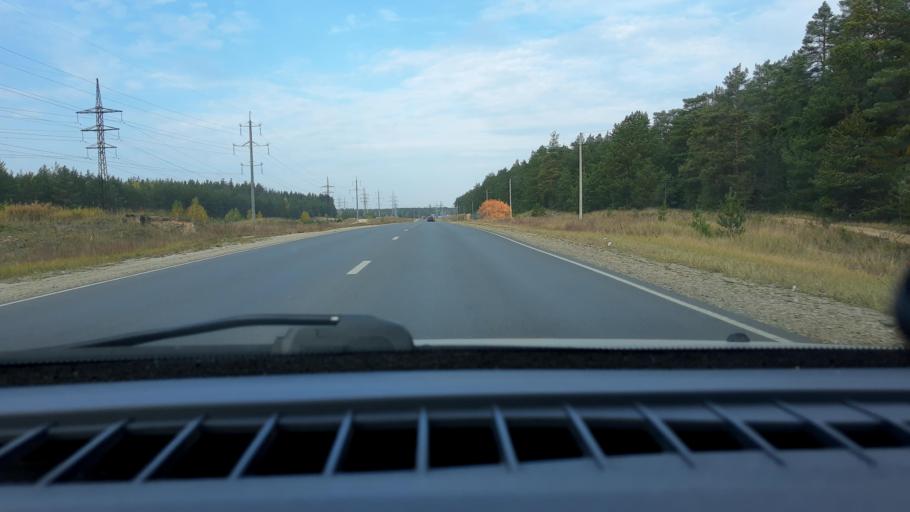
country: RU
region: Nizjnij Novgorod
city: Lukino
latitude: 56.3985
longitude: 43.6675
